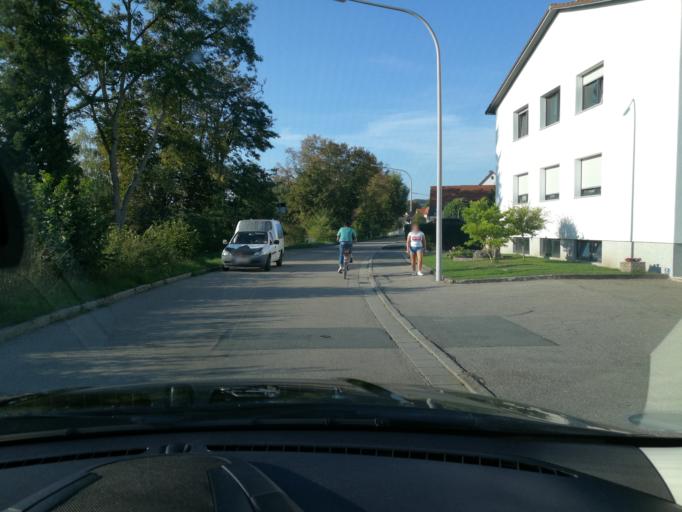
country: DE
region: Bavaria
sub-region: Upper Palatinate
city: Velburg
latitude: 49.2285
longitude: 11.6710
